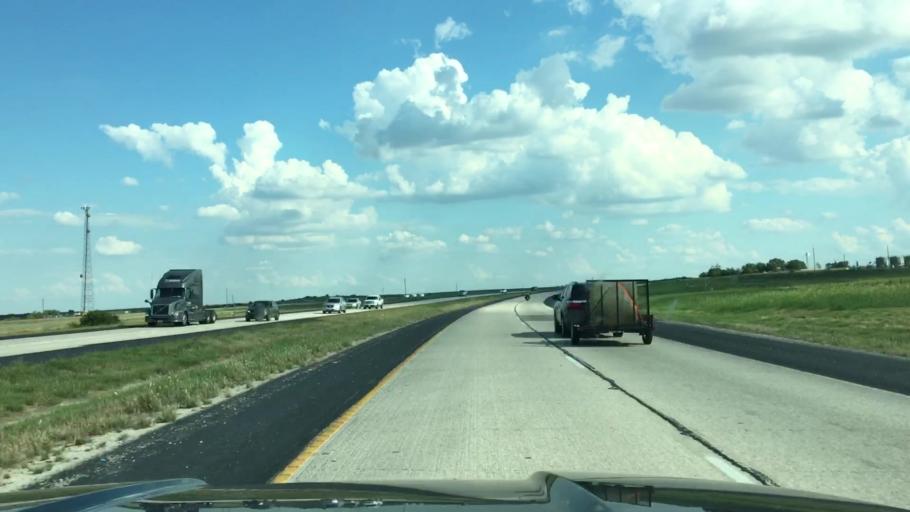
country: US
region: Texas
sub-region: Wise County
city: New Fairview
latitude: 33.1461
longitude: -97.5019
